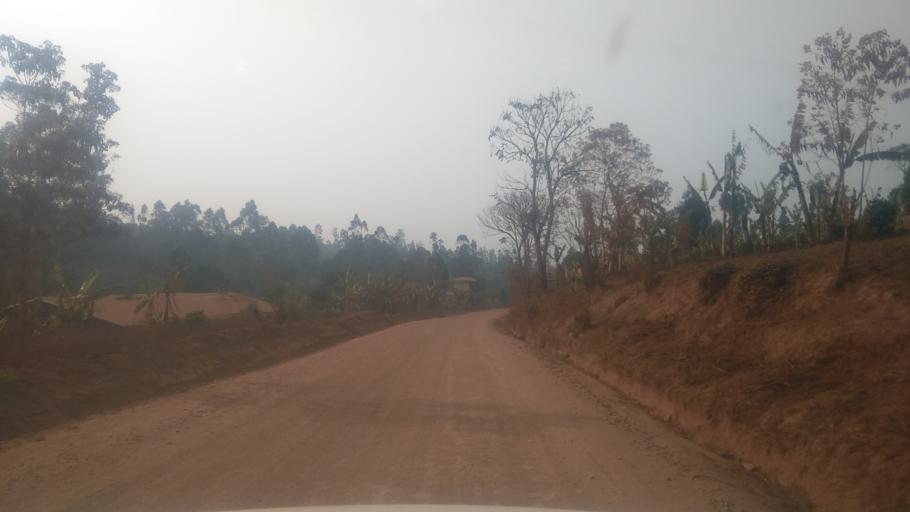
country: CM
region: West
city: Dschang
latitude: 5.4795
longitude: 10.1082
